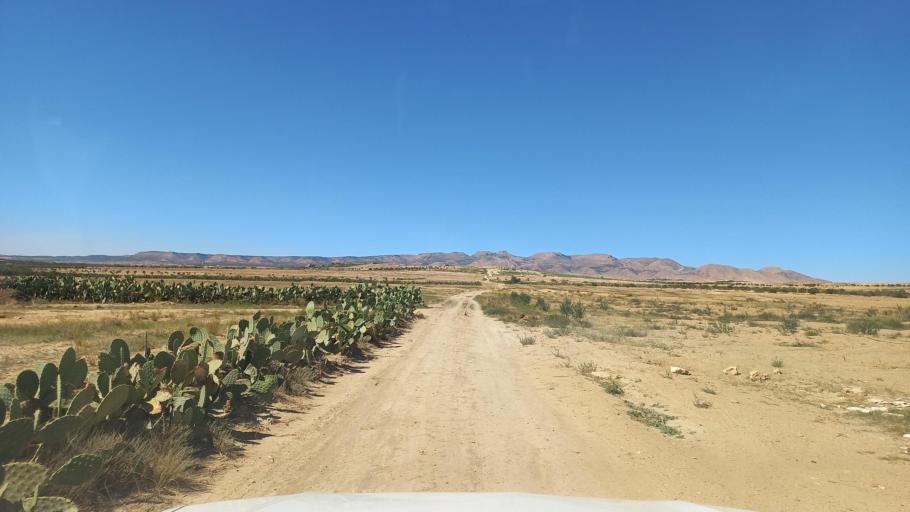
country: TN
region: Al Qasrayn
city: Sbiba
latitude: 35.3690
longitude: 9.0852
